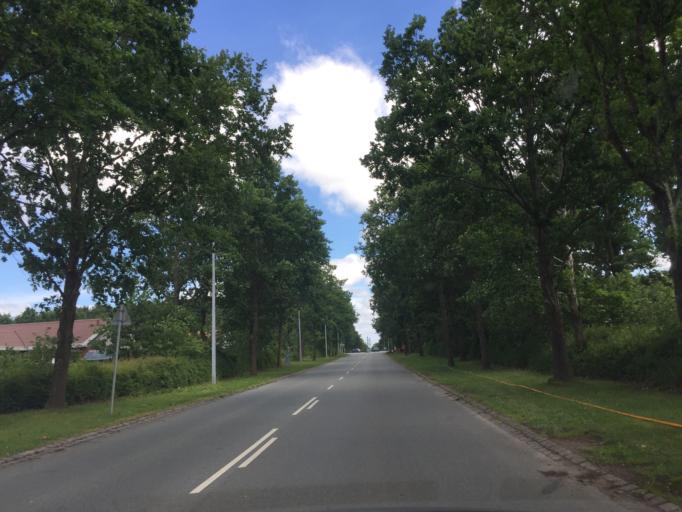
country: DK
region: South Denmark
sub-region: Odense Kommune
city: Neder Holluf
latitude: 55.3658
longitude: 10.4523
